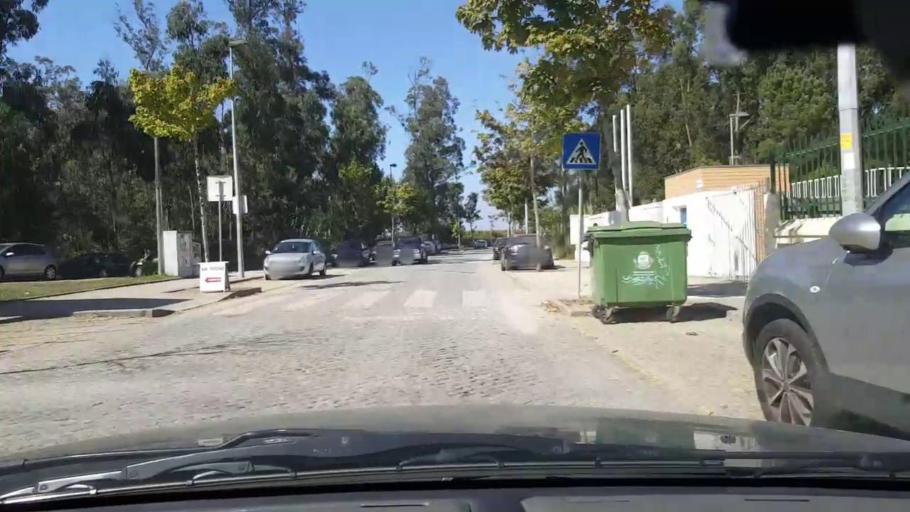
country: PT
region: Porto
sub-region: Vila do Conde
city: Arvore
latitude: 41.3091
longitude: -8.7206
